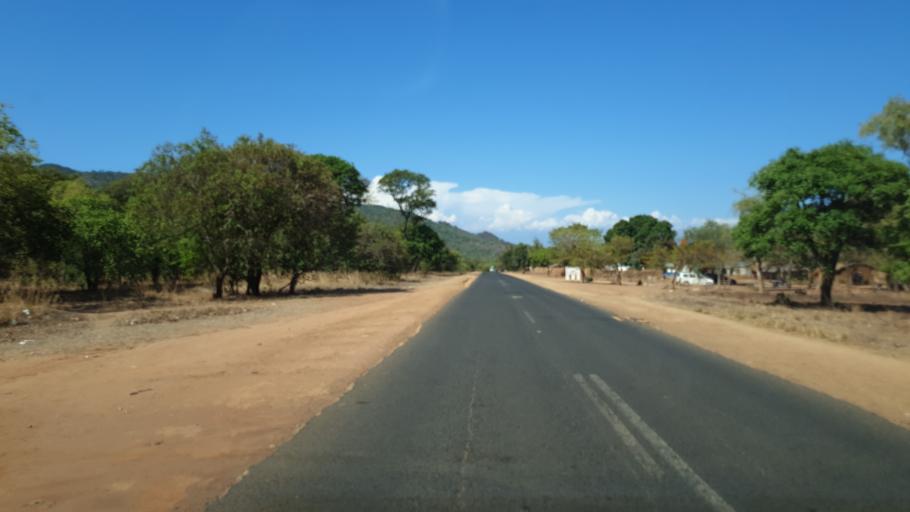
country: MW
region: Central Region
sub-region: Salima District
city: Salima
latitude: -13.7368
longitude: 34.5984
